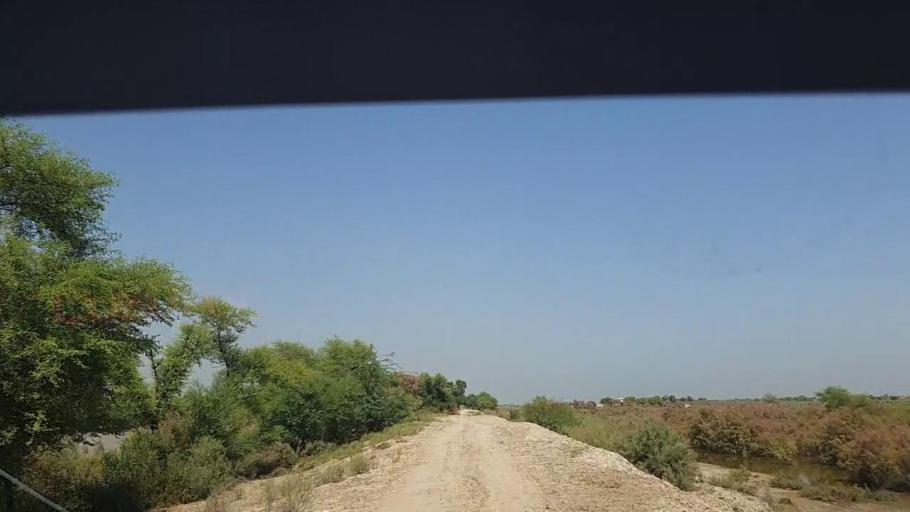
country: PK
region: Sindh
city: Kandhkot
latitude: 28.1771
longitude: 69.1495
